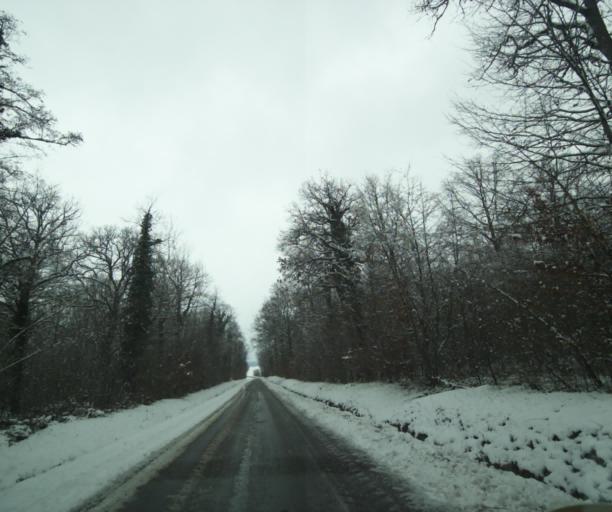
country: FR
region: Champagne-Ardenne
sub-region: Departement de la Haute-Marne
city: Laneuville-a-Remy
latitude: 48.3928
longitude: 4.8679
